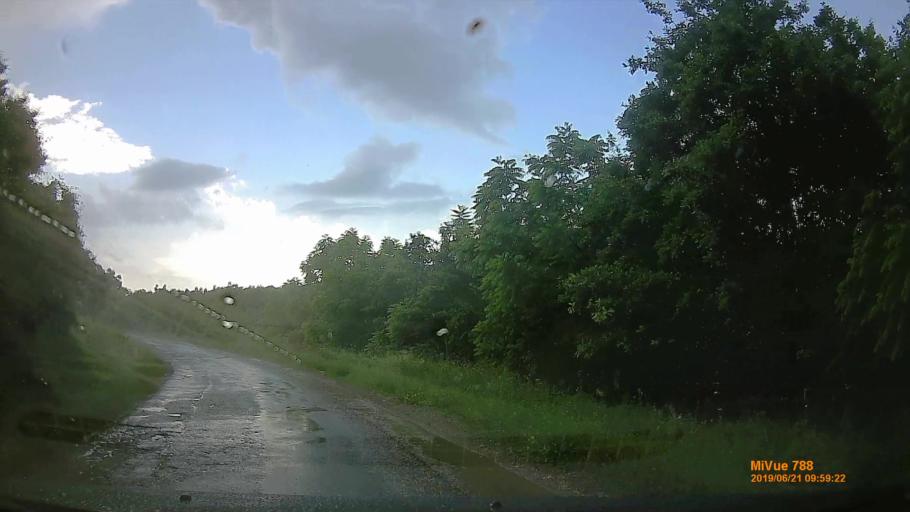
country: HU
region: Baranya
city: Buekkoesd
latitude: 46.2121
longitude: 17.9706
